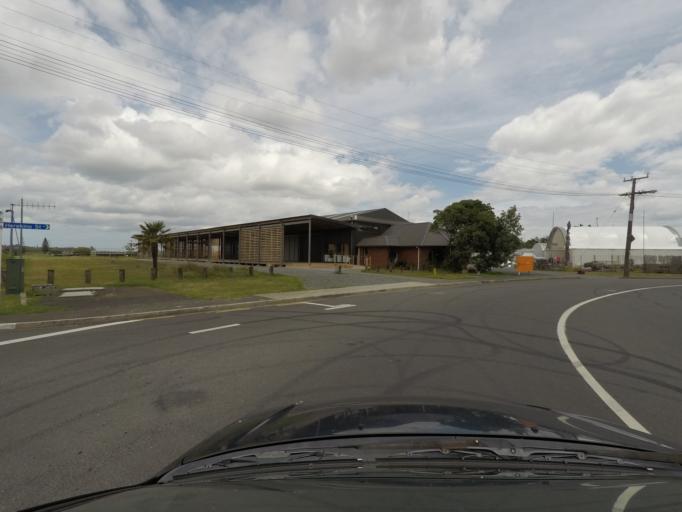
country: NZ
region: Northland
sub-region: Whangarei
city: Whangarei
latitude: -35.7285
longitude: 174.3310
